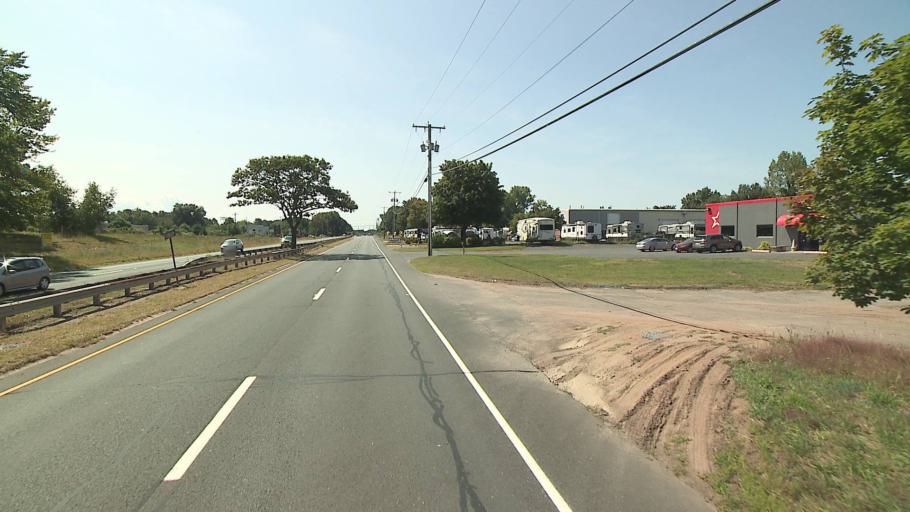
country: US
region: Connecticut
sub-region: Hartford County
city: South Windsor
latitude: 41.8141
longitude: -72.6115
